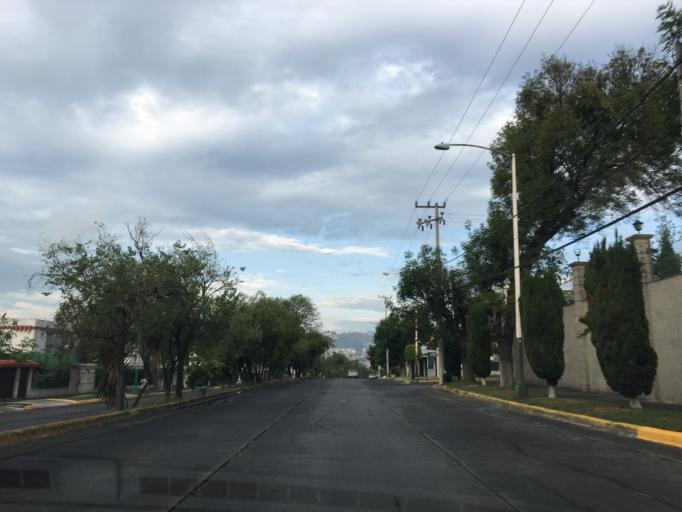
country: MX
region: Mexico
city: Naucalpan de Juarez
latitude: 19.5024
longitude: -99.2391
